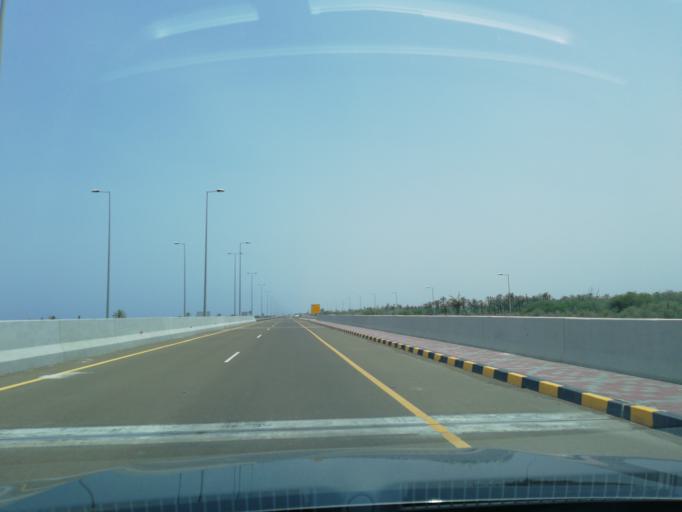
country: OM
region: Al Batinah
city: Al Liwa'
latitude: 24.6382
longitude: 56.5224
